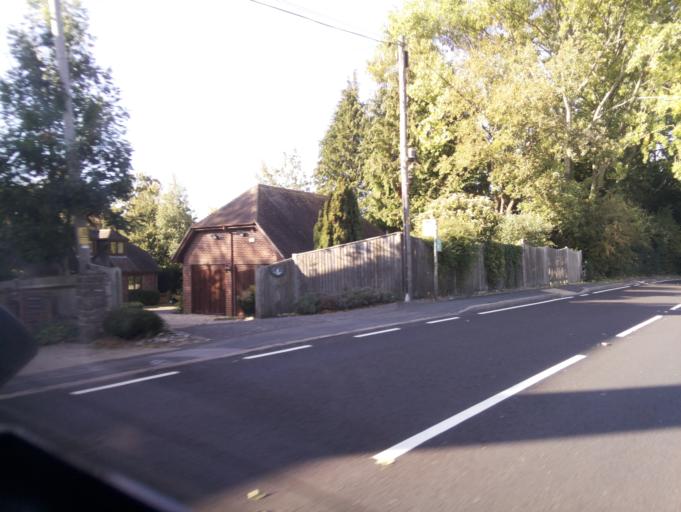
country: GB
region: England
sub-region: Hampshire
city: Swanmore
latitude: 50.9810
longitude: -1.1302
